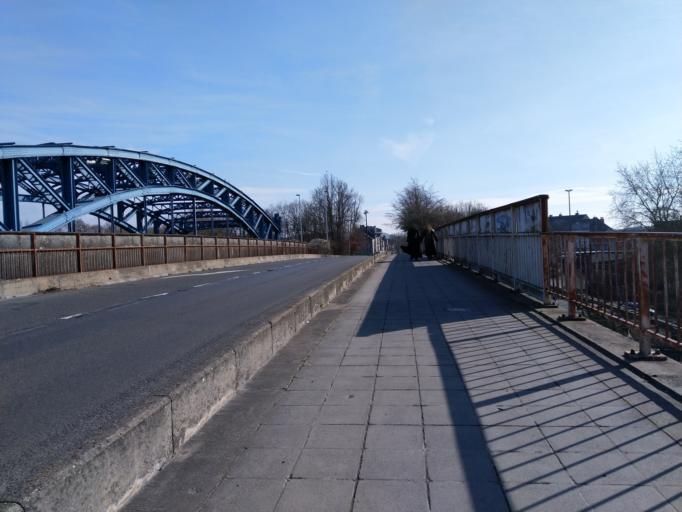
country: BE
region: Wallonia
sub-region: Province du Hainaut
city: Mons
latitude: 50.4503
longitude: 3.9370
